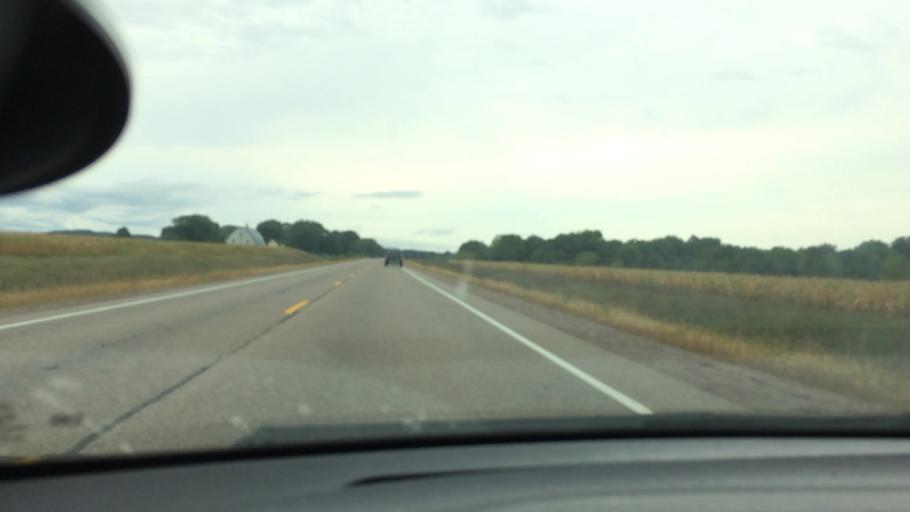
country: US
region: Wisconsin
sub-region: Trempealeau County
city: Osseo
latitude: 44.5863
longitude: -91.1370
